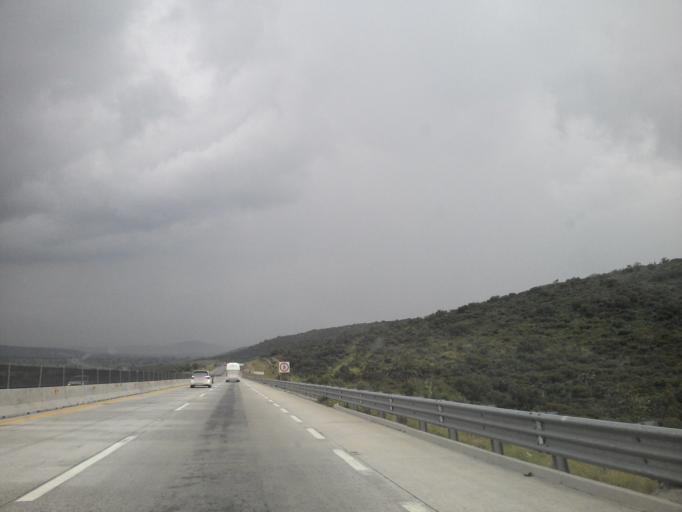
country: MX
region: Morelos
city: San Francisco Zacacalco
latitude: 19.9605
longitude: -98.9988
